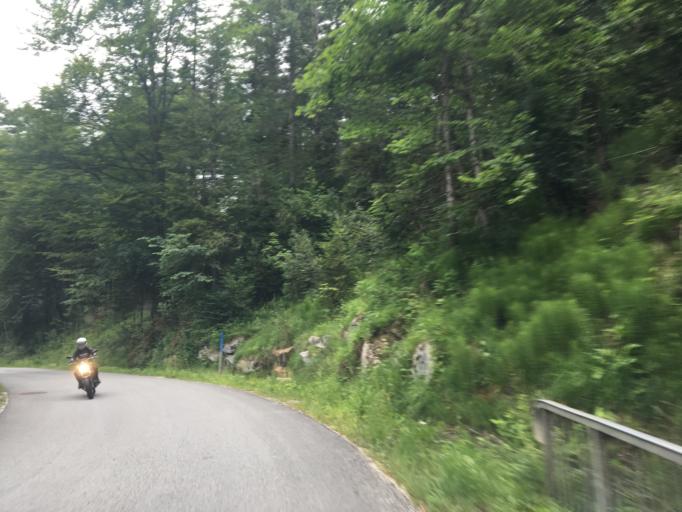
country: AT
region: Salzburg
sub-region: Politischer Bezirk Salzburg-Umgebung
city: Strobl
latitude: 47.6922
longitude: 13.4877
